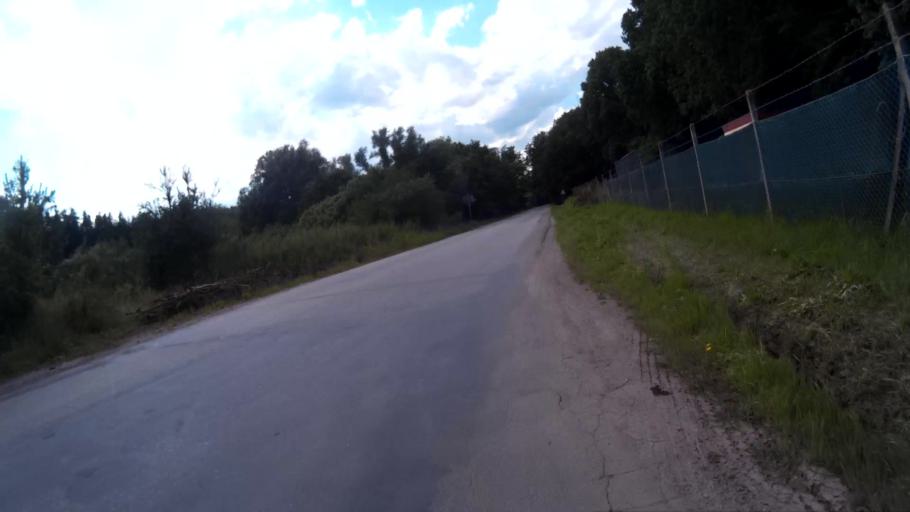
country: CZ
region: South Moravian
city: Strelice
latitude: 49.1501
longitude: 16.4634
